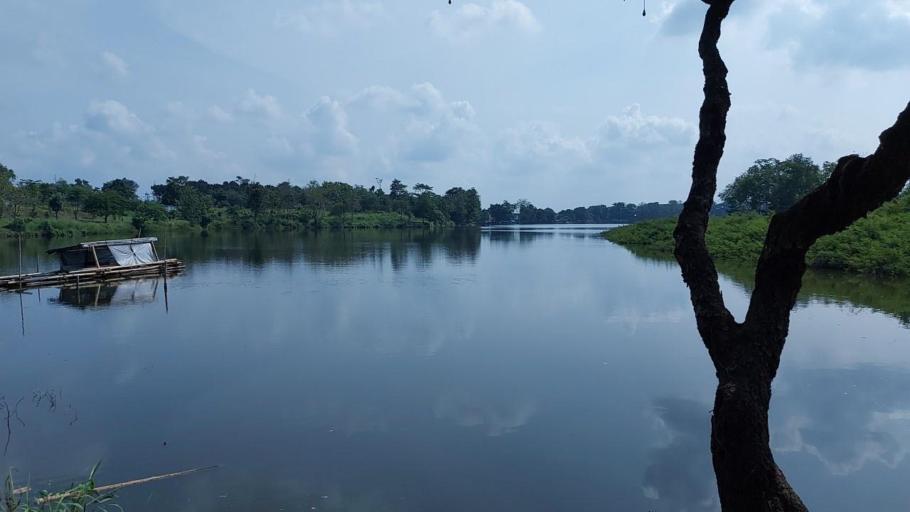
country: ID
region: West Java
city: Cibinong
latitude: -6.4733
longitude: 106.8333
